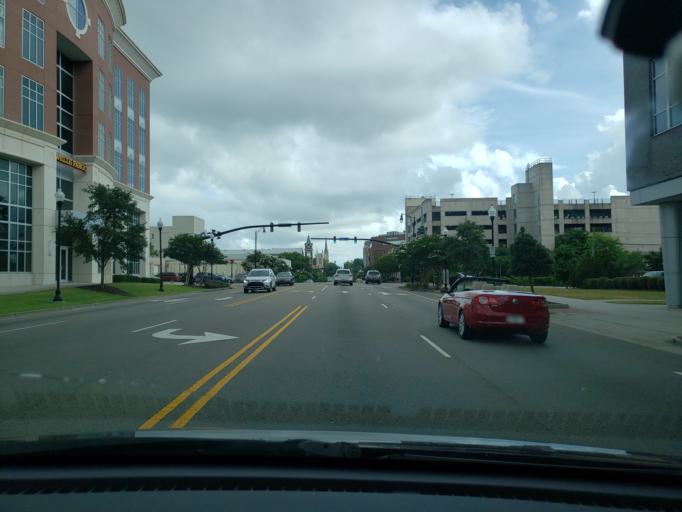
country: US
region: North Carolina
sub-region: New Hanover County
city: Wilmington
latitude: 34.2396
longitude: -77.9466
